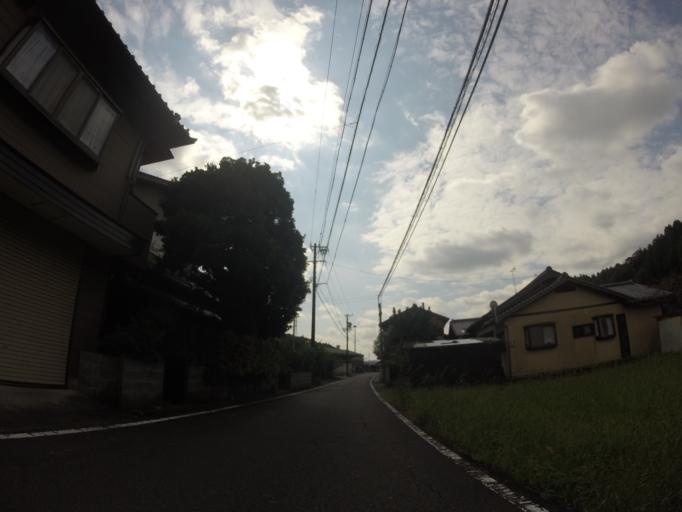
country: JP
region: Shizuoka
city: Kanaya
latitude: 34.8669
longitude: 138.1322
